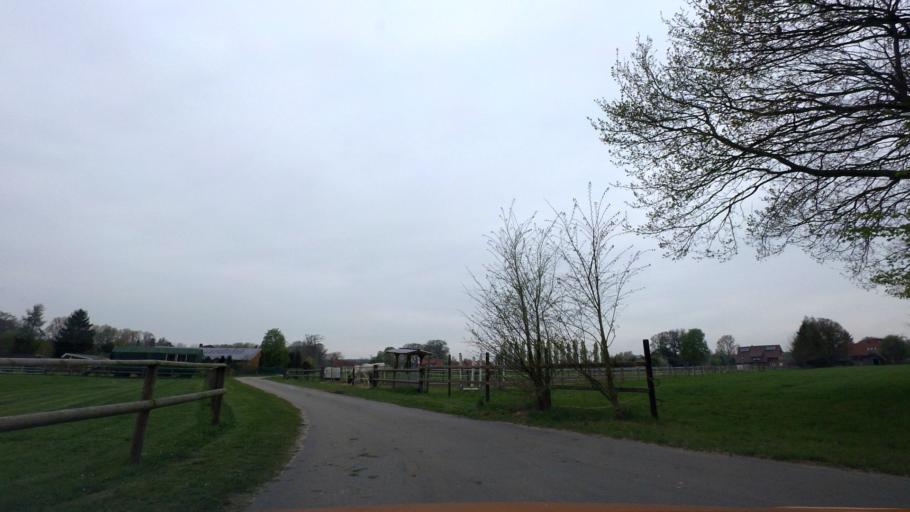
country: DE
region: Lower Saxony
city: Bramsche
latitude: 52.4353
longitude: 7.9737
